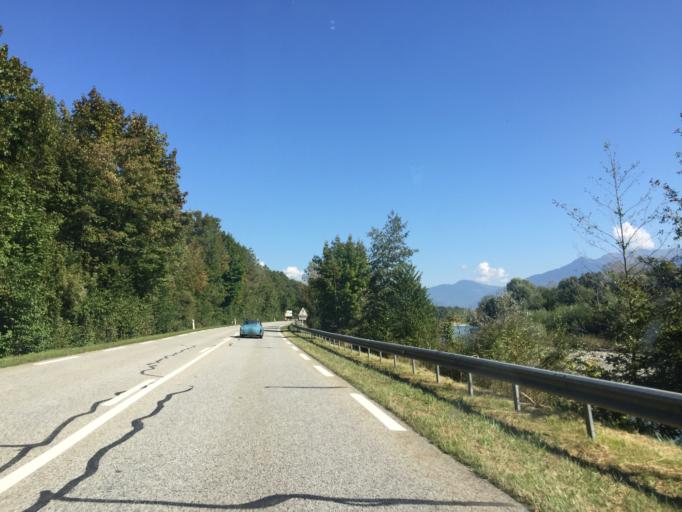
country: FR
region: Rhone-Alpes
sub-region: Departement de la Savoie
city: Gresy-sur-Isere
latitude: 45.6042
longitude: 6.2800
